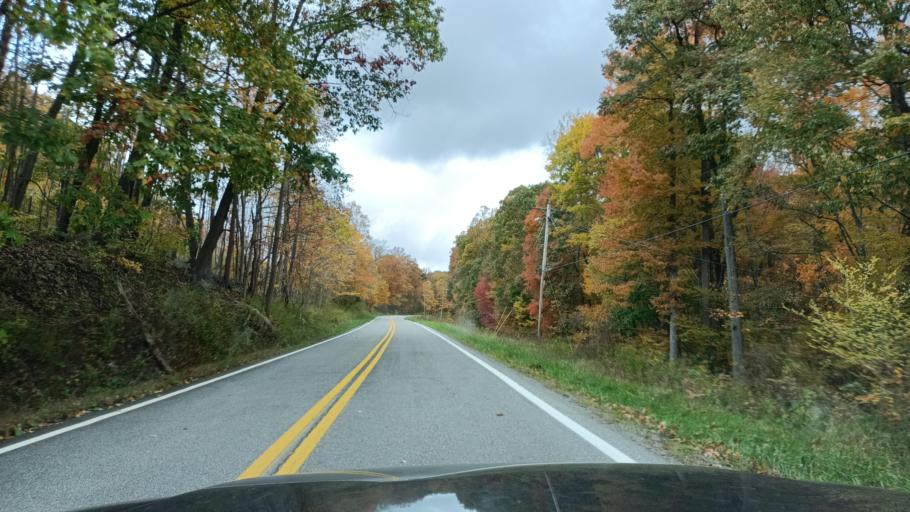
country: US
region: West Virginia
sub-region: Monongalia County
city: Cheat Lake
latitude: 39.6559
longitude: -79.7583
